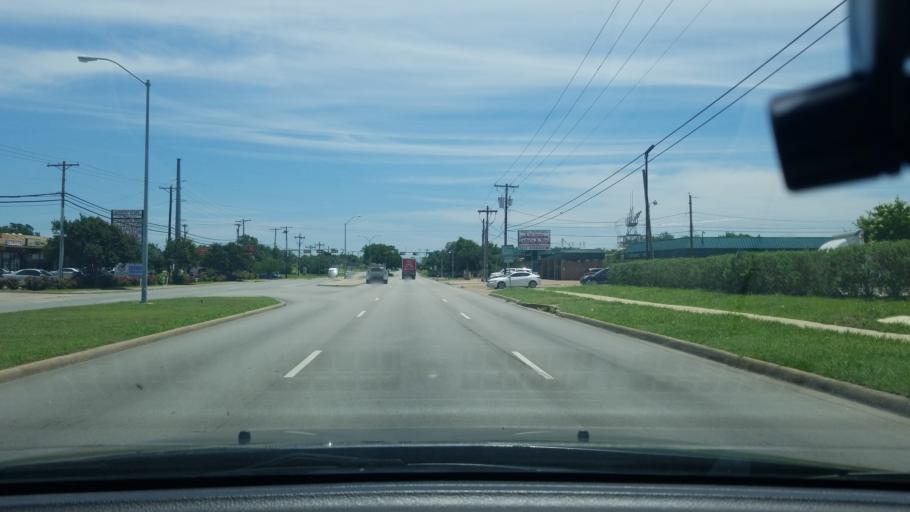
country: US
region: Texas
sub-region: Dallas County
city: Mesquite
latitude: 32.7770
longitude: -96.6196
